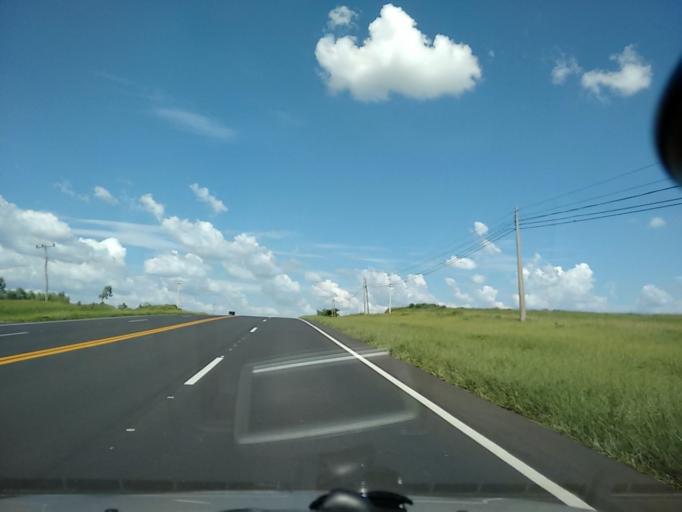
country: BR
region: Sao Paulo
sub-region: Pompeia
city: Pompeia
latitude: -22.1015
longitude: -50.2297
